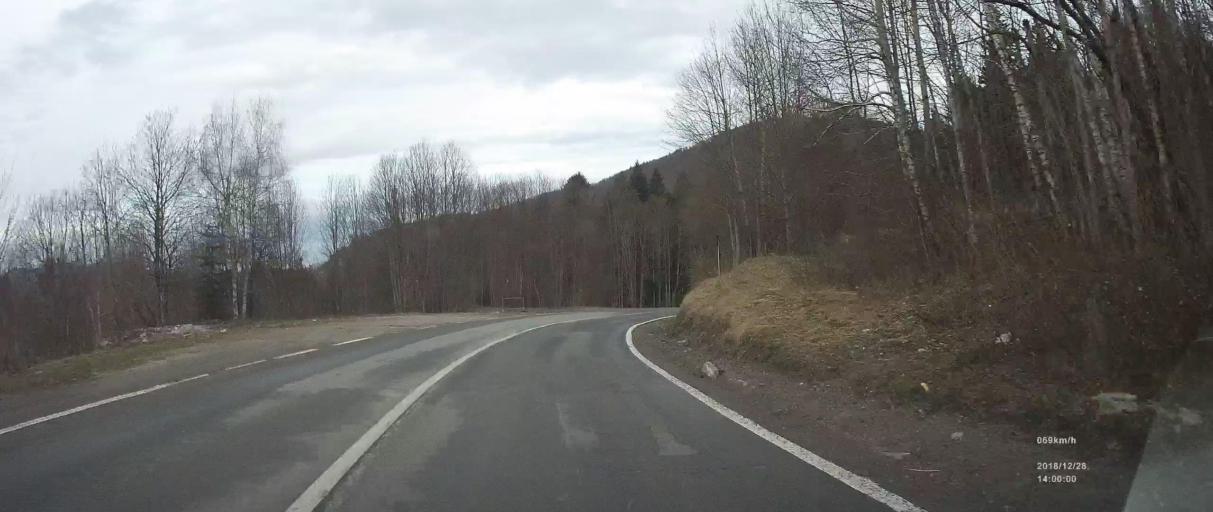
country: SI
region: Kostel
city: Kostel
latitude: 45.4075
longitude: 14.9137
